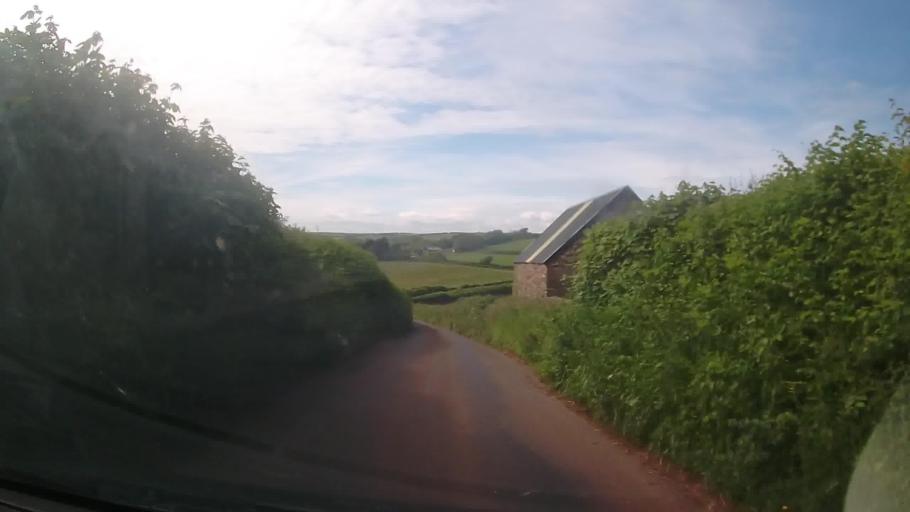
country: GB
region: England
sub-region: Devon
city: Salcombe
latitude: 50.2382
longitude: -3.6768
